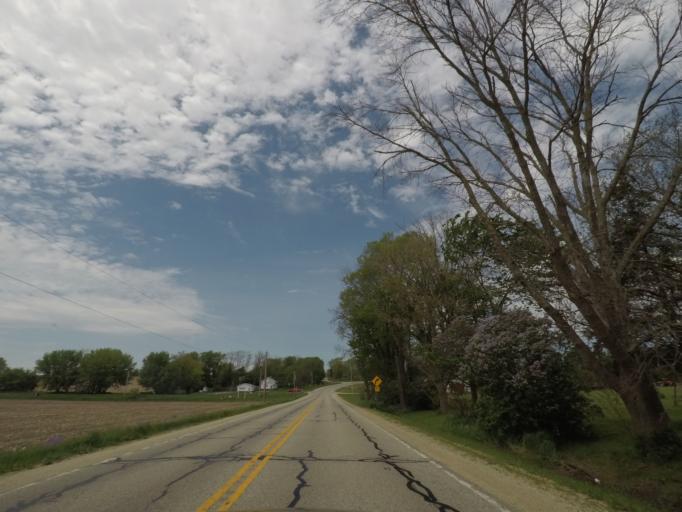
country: US
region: Wisconsin
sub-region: Rock County
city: Orfordville
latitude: 42.5995
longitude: -89.2066
